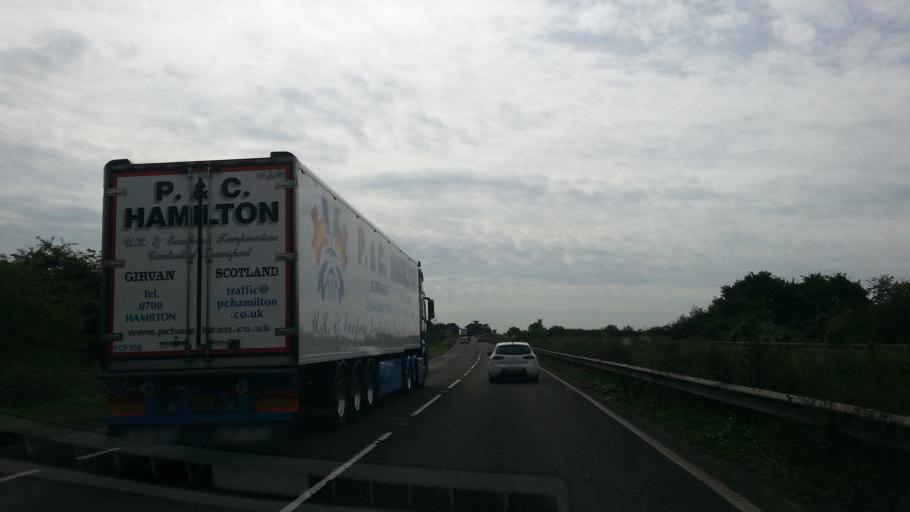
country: GB
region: England
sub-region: Central Bedfordshire
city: Astwick
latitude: 52.0267
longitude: -0.2129
